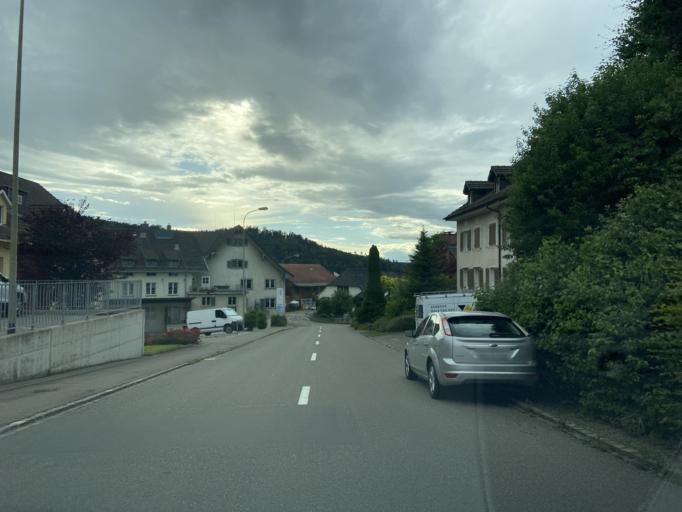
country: CH
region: Zurich
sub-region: Bezirk Winterthur
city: Elgg / Staedtchen und Umgebung
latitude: 47.4922
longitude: 8.8654
